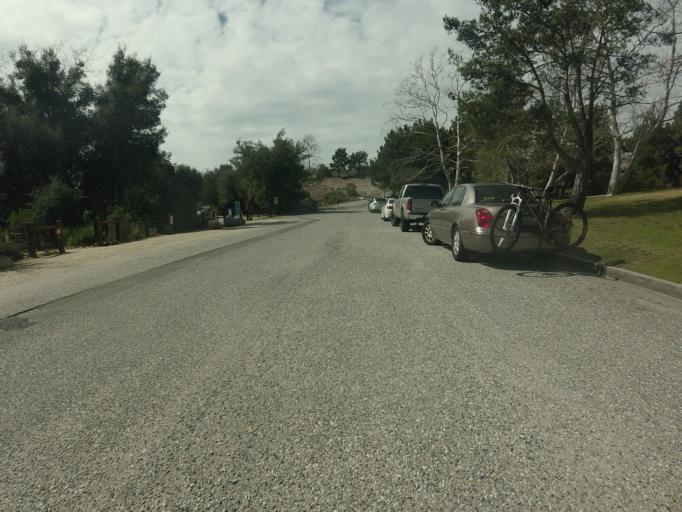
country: US
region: California
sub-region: Orange County
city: Aliso Viejo
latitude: 33.5519
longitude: -117.7200
